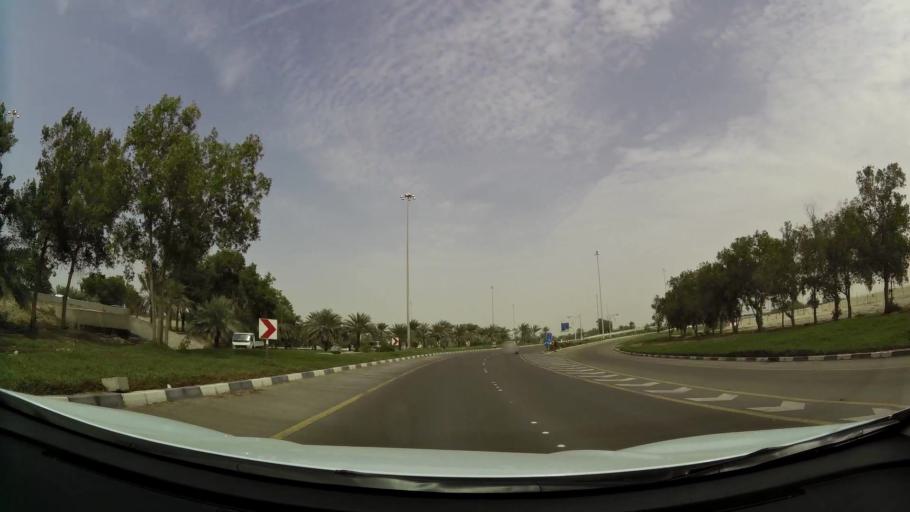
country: AE
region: Abu Dhabi
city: Abu Dhabi
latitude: 24.3904
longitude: 54.5268
